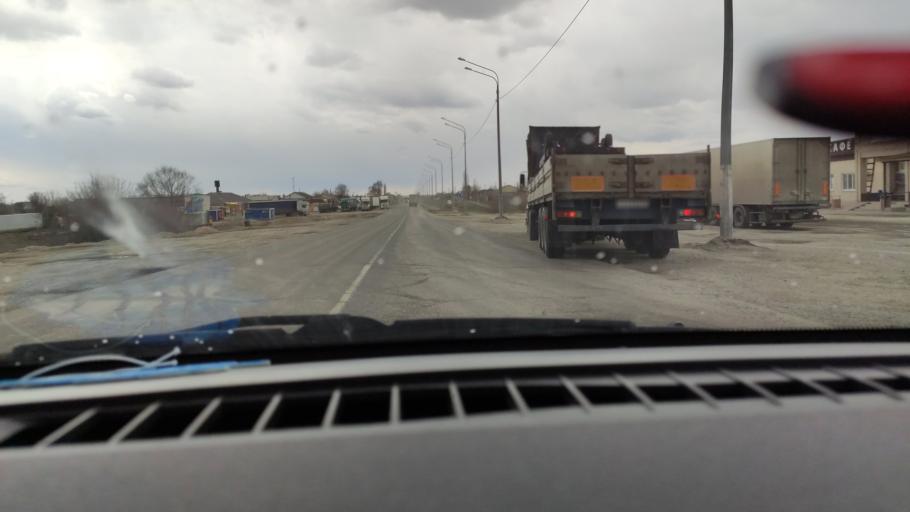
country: RU
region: Saratov
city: Sinodskoye
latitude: 51.9943
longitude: 46.6718
